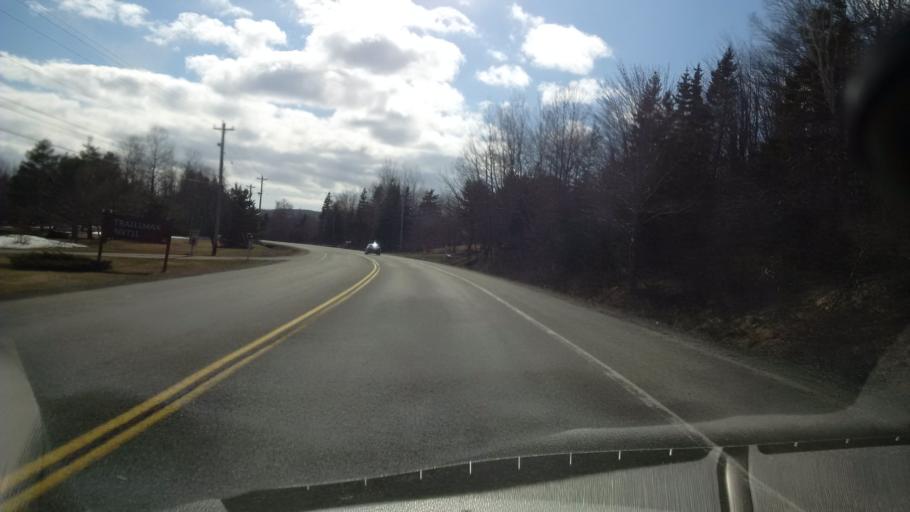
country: CA
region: Nova Scotia
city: Princeville
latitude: 46.0952
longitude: -60.8833
